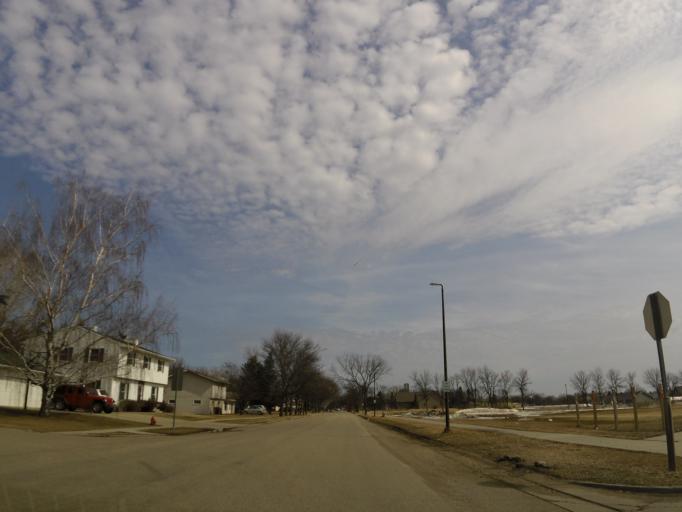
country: US
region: North Dakota
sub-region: Walsh County
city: Grafton
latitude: 48.4081
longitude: -97.4224
